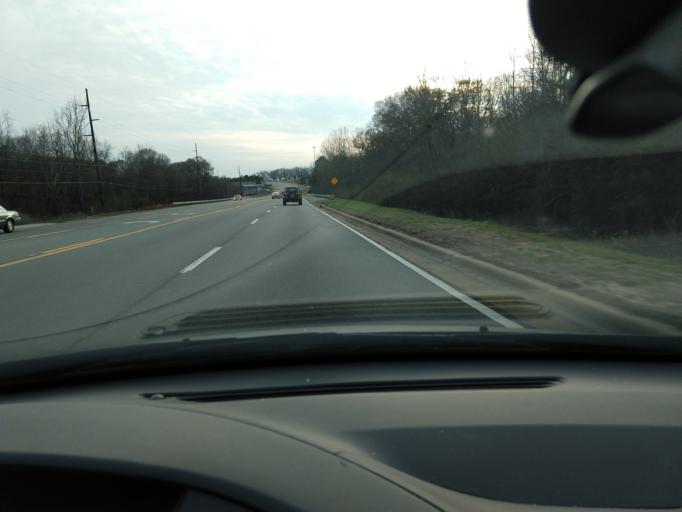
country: US
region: Georgia
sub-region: Sumter County
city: Americus
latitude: 32.0719
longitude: -84.2466
